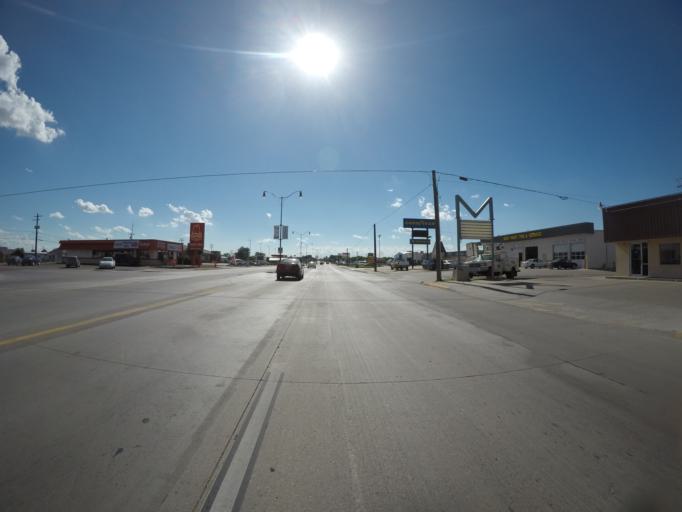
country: US
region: Colorado
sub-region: Logan County
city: Sterling
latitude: 40.6253
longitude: -103.2252
